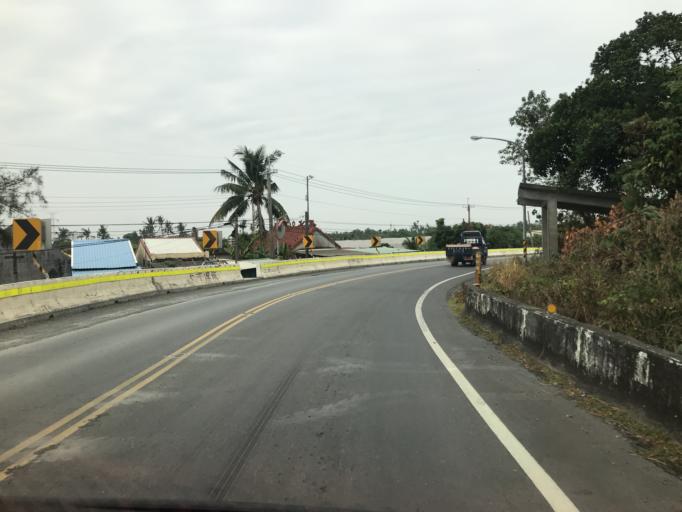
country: TW
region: Taiwan
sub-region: Pingtung
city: Pingtung
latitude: 22.4954
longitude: 120.5908
